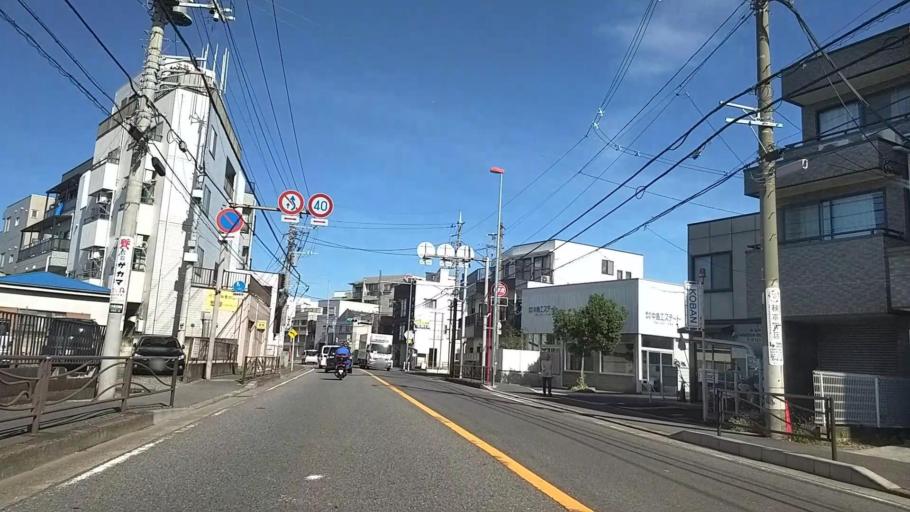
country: JP
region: Kanagawa
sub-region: Kawasaki-shi
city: Kawasaki
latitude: 35.5619
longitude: 139.6498
